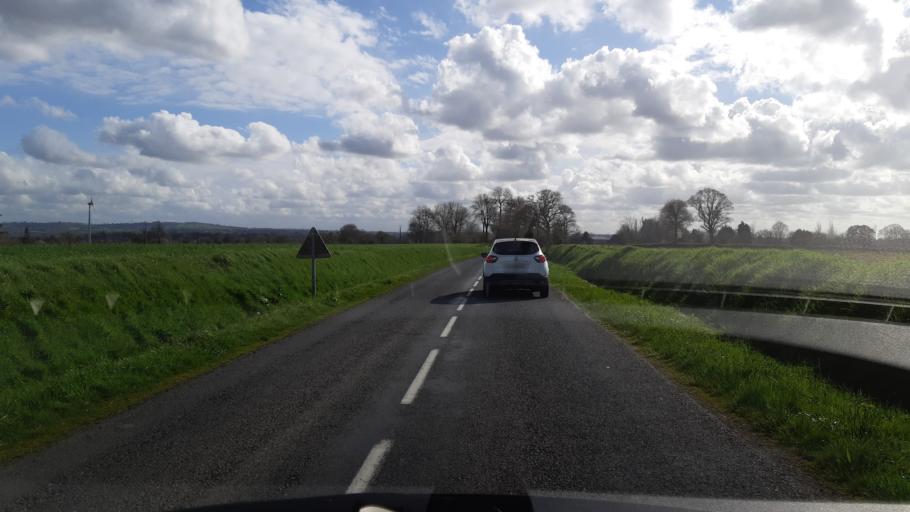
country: FR
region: Lower Normandy
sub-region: Departement de la Manche
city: Percy
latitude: 49.0174
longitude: -1.1630
